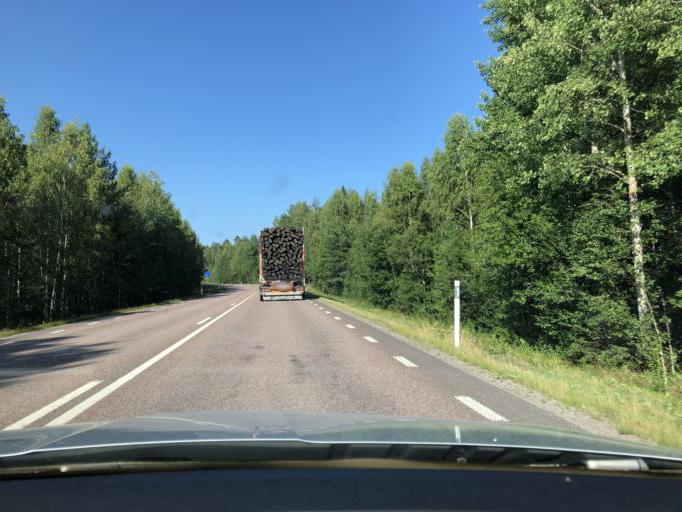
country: SE
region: Dalarna
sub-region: Faluns Kommun
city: Falun
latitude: 60.5789
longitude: 15.7737
